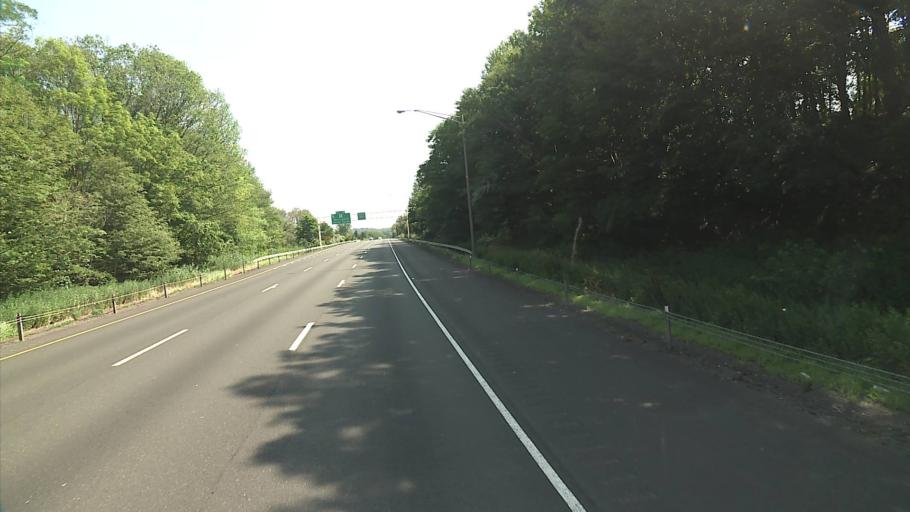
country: US
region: Connecticut
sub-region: New Haven County
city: Wallingford Center
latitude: 41.4194
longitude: -72.8270
